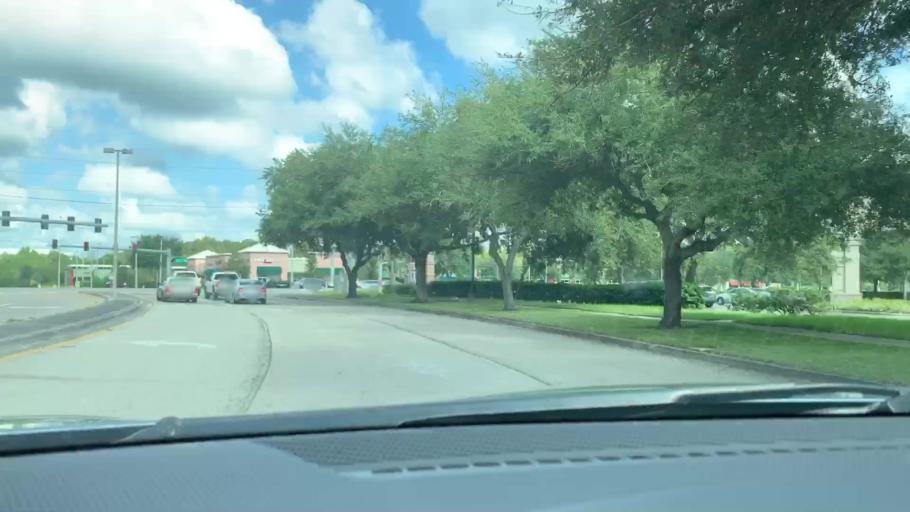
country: US
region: Florida
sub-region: Hillsborough County
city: Pebble Creek
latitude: 28.1260
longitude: -82.3687
